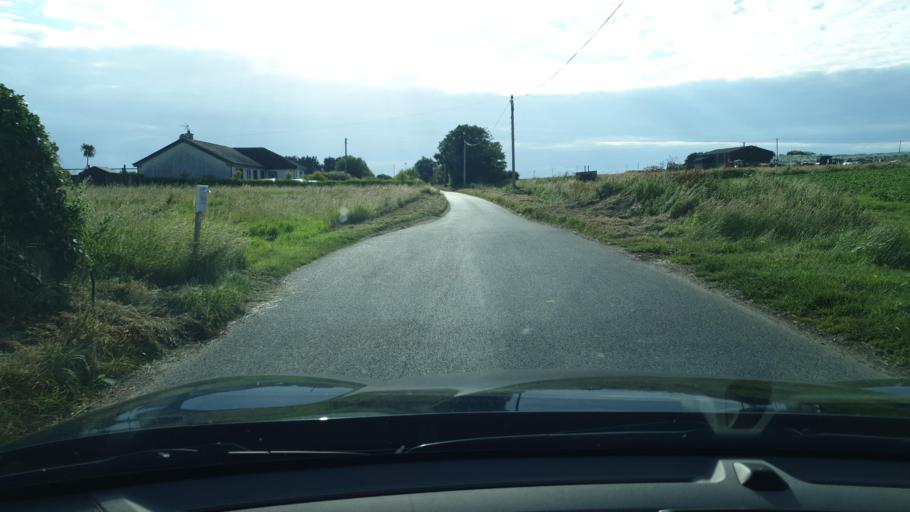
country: IE
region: Leinster
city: An Ros
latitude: 53.5326
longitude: -6.0987
